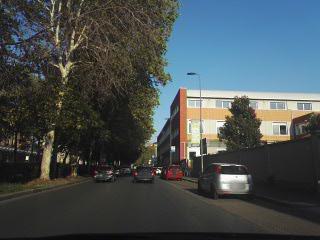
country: IT
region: Lombardy
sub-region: Citta metropolitana di Milano
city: Milano
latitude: 45.4439
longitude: 9.1700
